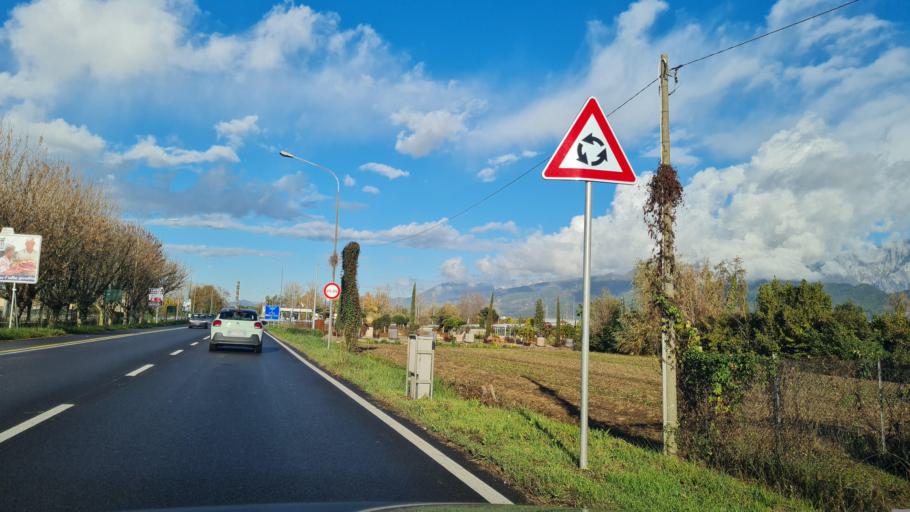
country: IT
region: Tuscany
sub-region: Provincia di Lucca
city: Pietrasanta
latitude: 43.9497
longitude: 10.2033
